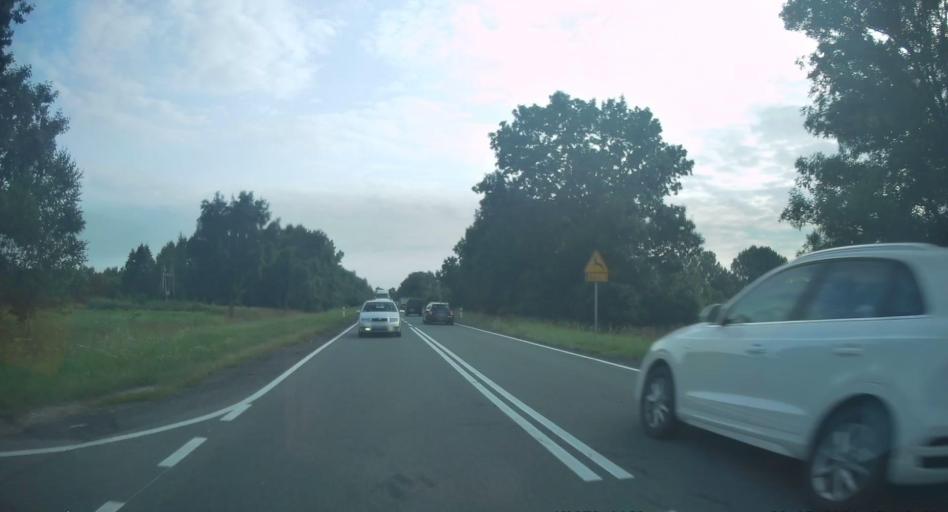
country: PL
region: Silesian Voivodeship
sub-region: Powiat czestochowski
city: Klomnice
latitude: 50.9354
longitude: 19.3844
